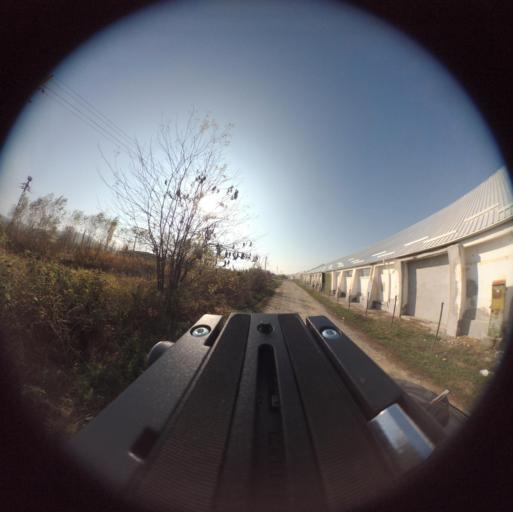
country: RO
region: Vaslui
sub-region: Comuna Dumesti
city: Dumesti
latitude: 46.8306
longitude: 27.2648
